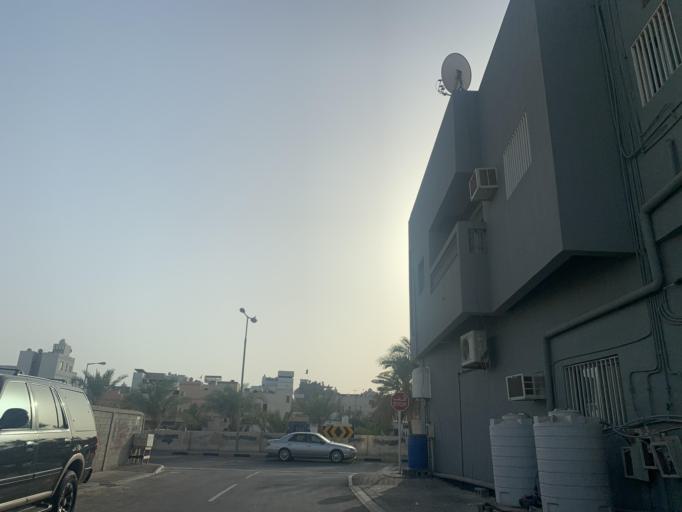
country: BH
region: Manama
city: Jidd Hafs
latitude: 26.2231
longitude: 50.5471
